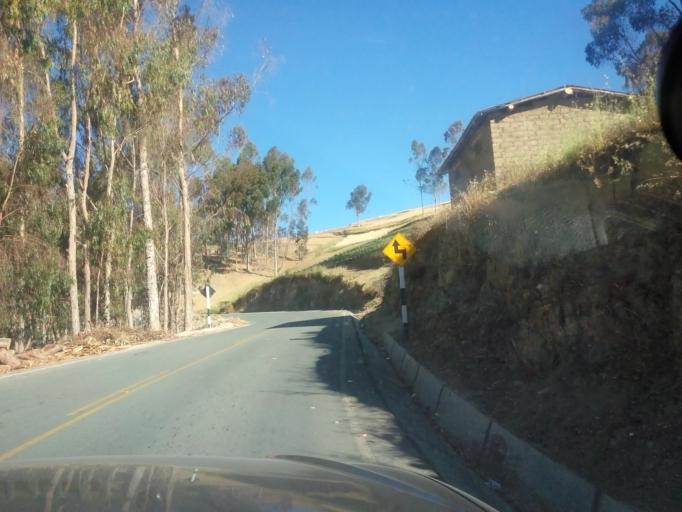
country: PE
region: Apurimac
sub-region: Provincia de Andahuaylas
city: Pacucha
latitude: -13.6545
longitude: -73.2940
